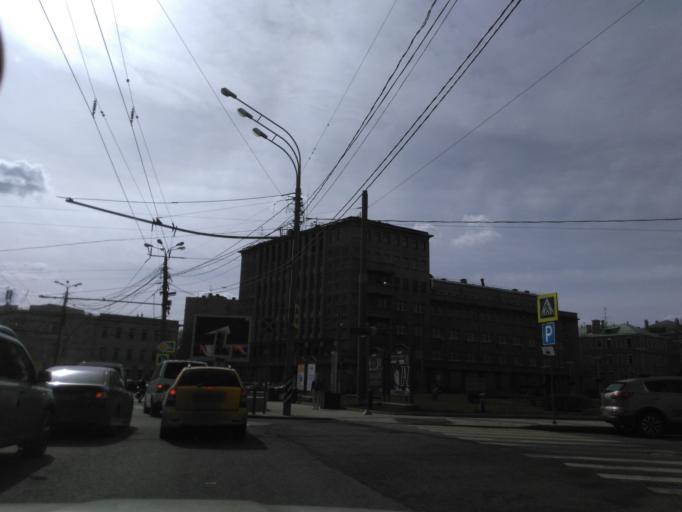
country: RU
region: Moskovskaya
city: Dorogomilovo
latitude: 55.7389
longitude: 37.5853
